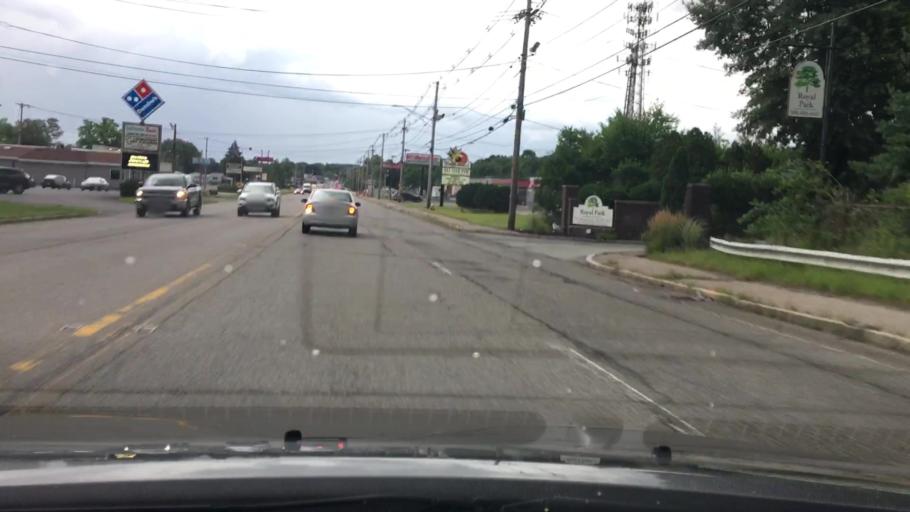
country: US
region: Massachusetts
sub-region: Norfolk County
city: Plainville
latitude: 41.9678
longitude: -71.3368
